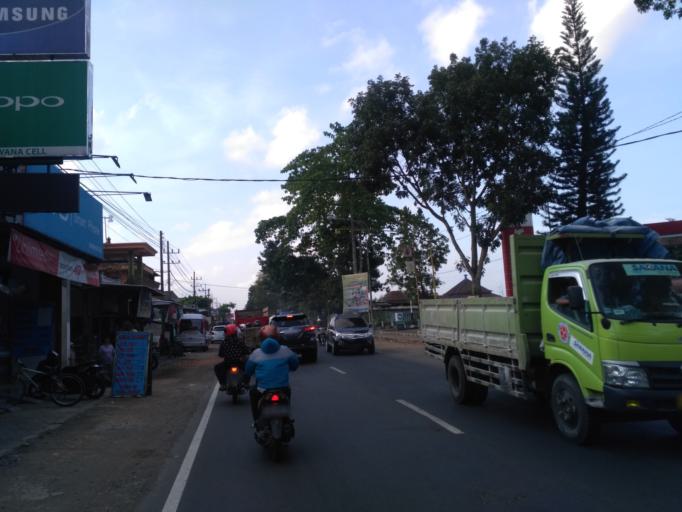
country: ID
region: East Java
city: Pakisaji
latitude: -8.0622
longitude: 112.6007
